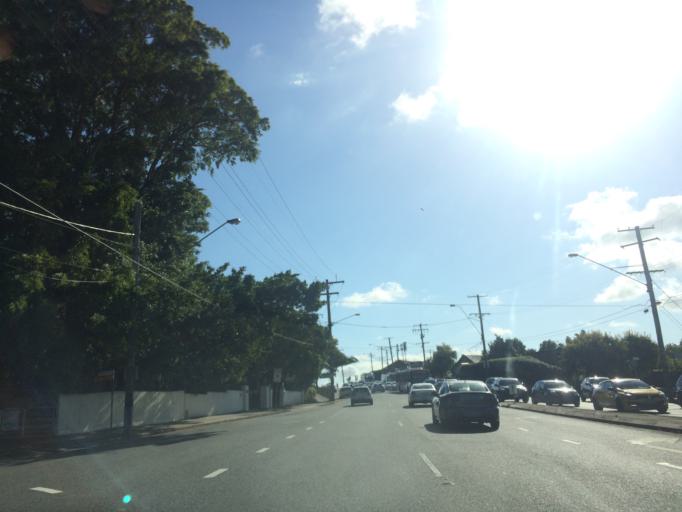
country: AU
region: Queensland
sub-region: Brisbane
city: Balmoral
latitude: -27.4734
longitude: 153.0573
